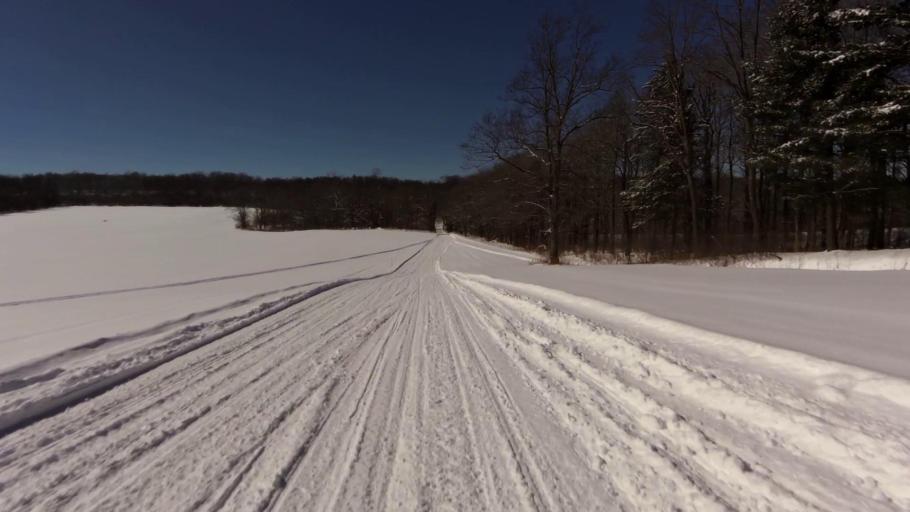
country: US
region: New York
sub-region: Chautauqua County
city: Mayville
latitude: 42.2171
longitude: -79.5219
